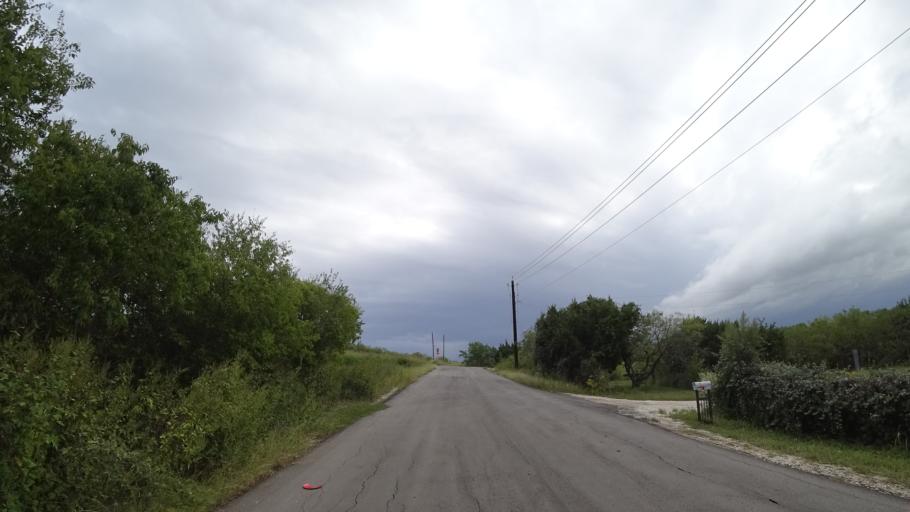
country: US
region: Texas
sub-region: Travis County
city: Onion Creek
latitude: 30.1510
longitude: -97.7321
